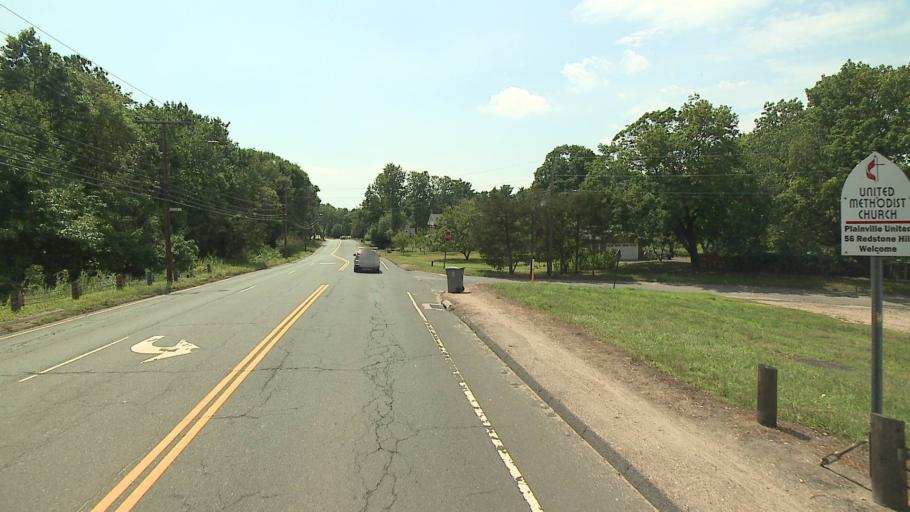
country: US
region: Connecticut
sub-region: Hartford County
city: Plainville
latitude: 41.6748
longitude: -72.8767
